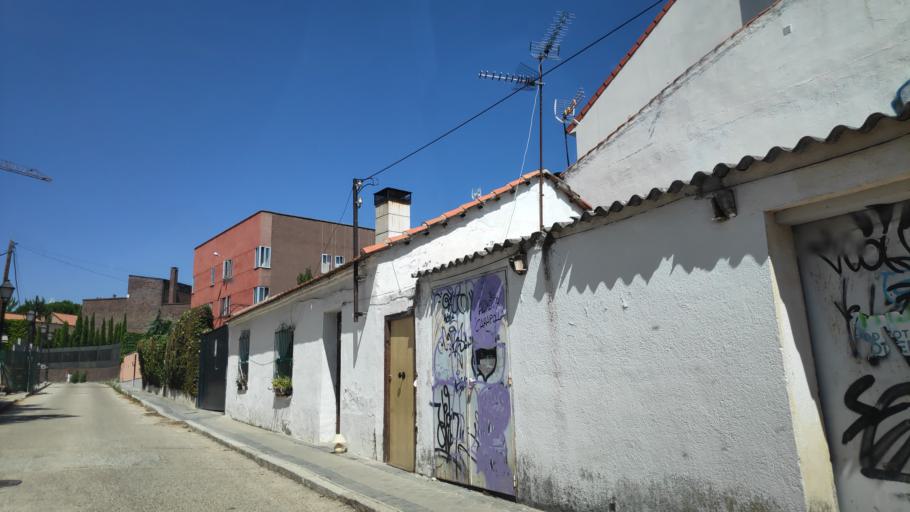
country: ES
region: Madrid
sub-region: Provincia de Madrid
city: Pozuelo de Alarcon
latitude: 40.4586
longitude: -3.7859
